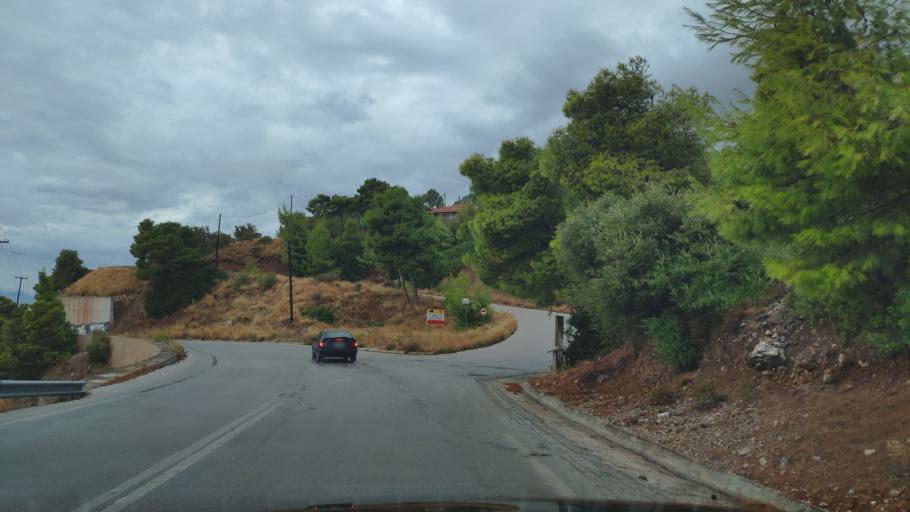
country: GR
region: Peloponnese
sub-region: Nomos Korinthias
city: Loutraki
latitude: 37.9847
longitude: 22.9683
